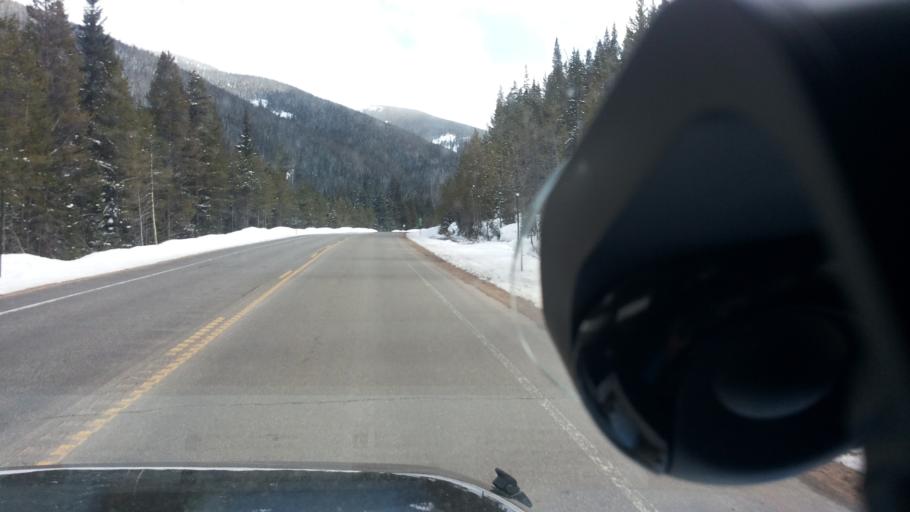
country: US
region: Colorado
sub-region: Grand County
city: Fraser
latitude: 39.8524
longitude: -105.7525
